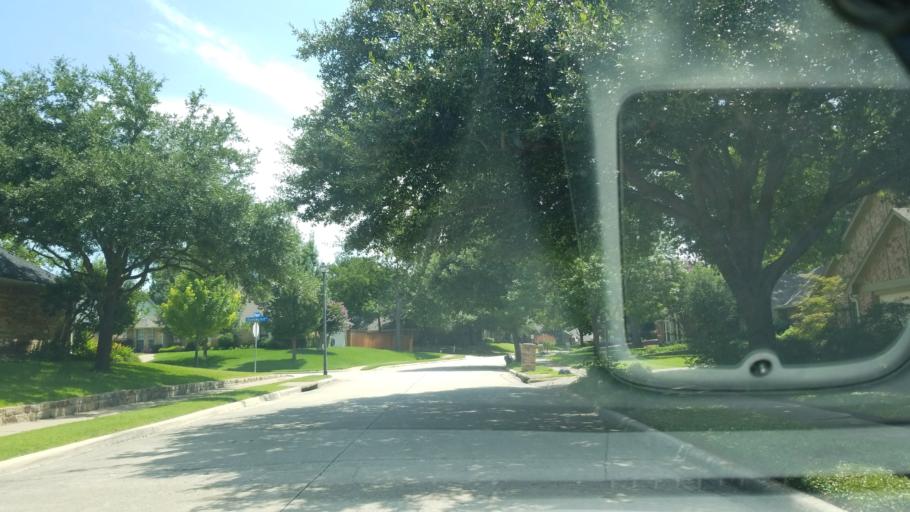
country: US
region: Texas
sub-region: Dallas County
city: Coppell
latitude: 32.9634
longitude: -96.9741
